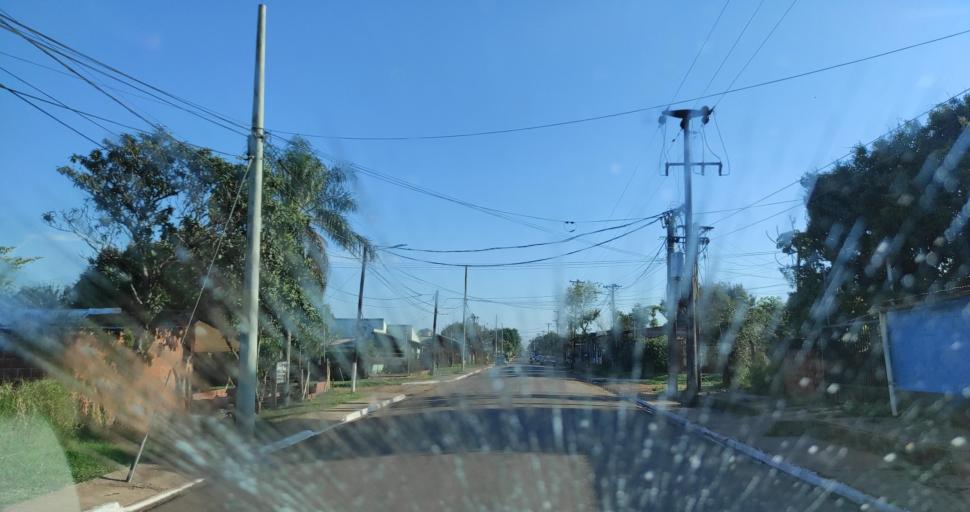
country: AR
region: Misiones
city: Garupa
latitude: -27.4445
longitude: -55.8562
